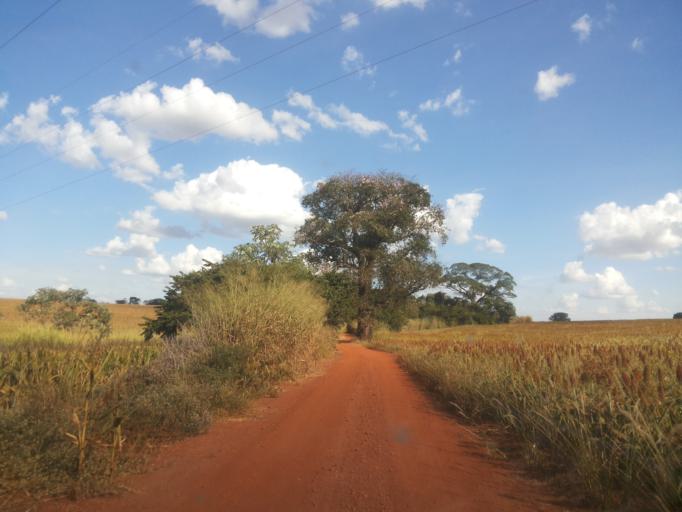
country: BR
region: Minas Gerais
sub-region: Capinopolis
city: Capinopolis
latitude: -18.5940
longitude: -49.4952
